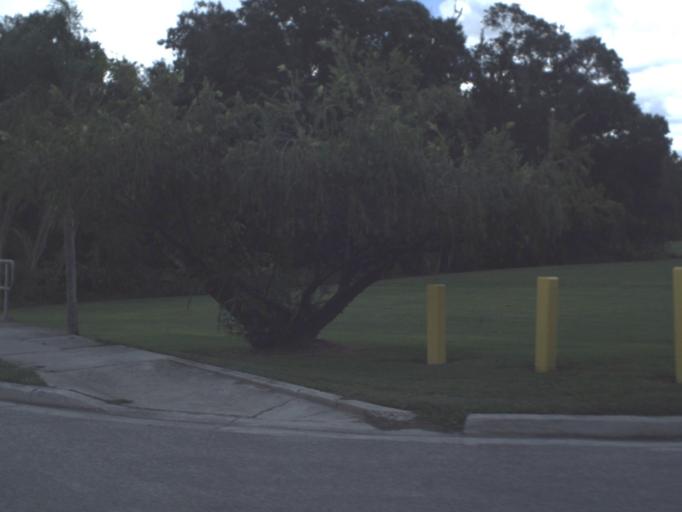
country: US
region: Florida
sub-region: Hillsborough County
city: Plant City
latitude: 28.0305
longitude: -82.1048
